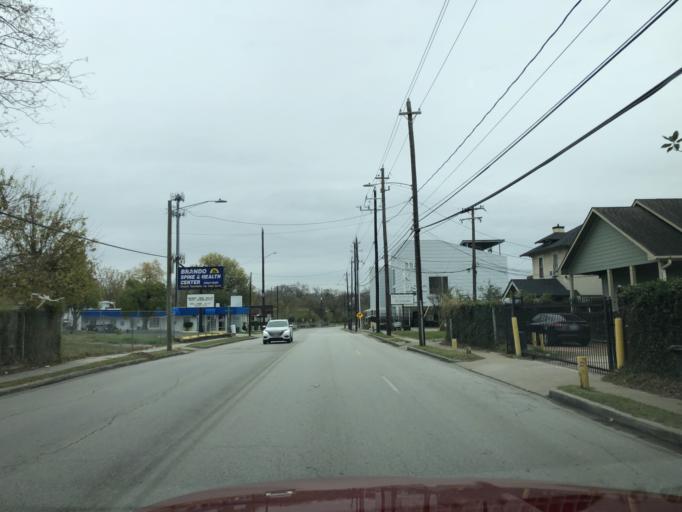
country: US
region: Texas
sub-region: Harris County
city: Houston
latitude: 29.7866
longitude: -95.3676
